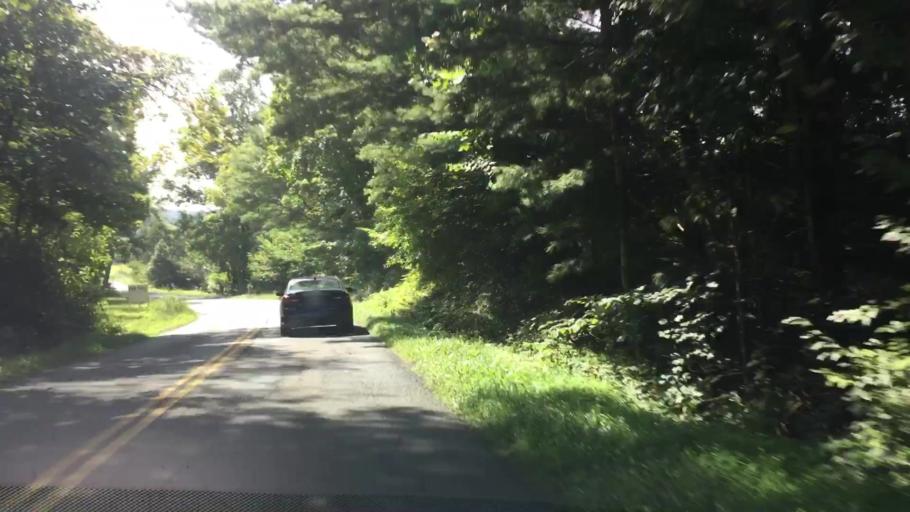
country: US
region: Tennessee
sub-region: Sullivan County
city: Fairmount
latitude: 36.6004
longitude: -82.0554
